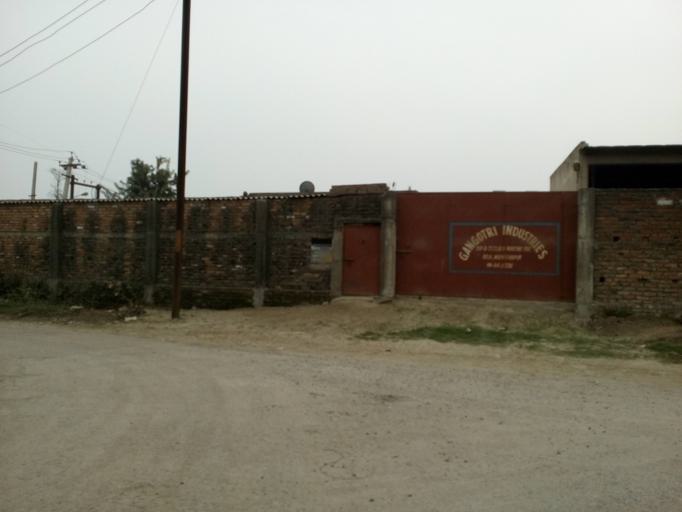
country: IN
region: Bihar
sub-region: Muzaffarpur
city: Muzaffarpur
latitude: 26.0996
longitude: 85.4065
